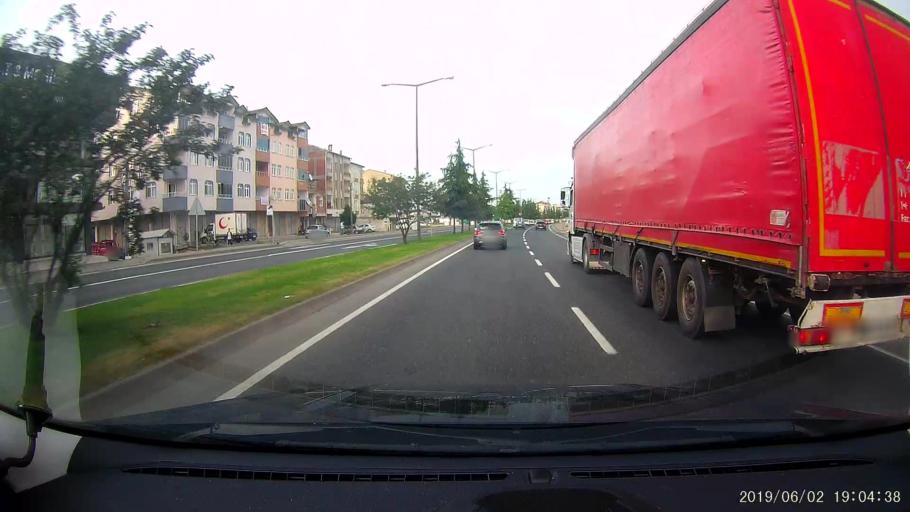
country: TR
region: Ordu
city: Ordu
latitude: 40.9770
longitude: 37.9427
